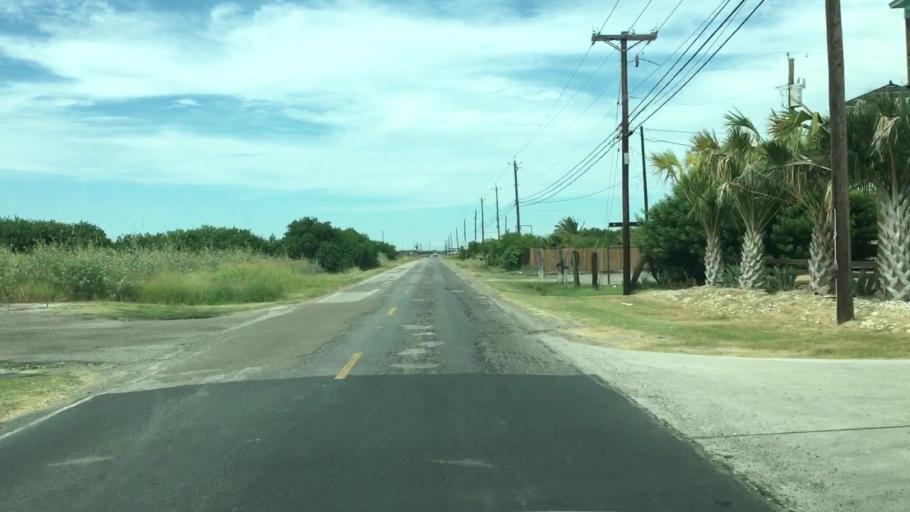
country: US
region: Texas
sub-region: Nueces County
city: Corpus Christi
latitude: 27.6313
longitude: -97.2905
